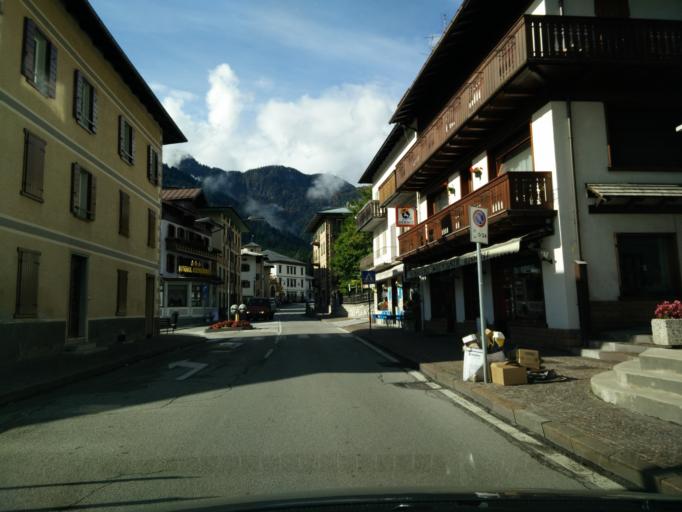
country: IT
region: Veneto
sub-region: Provincia di Belluno
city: Auronzo
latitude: 46.5527
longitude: 12.4393
